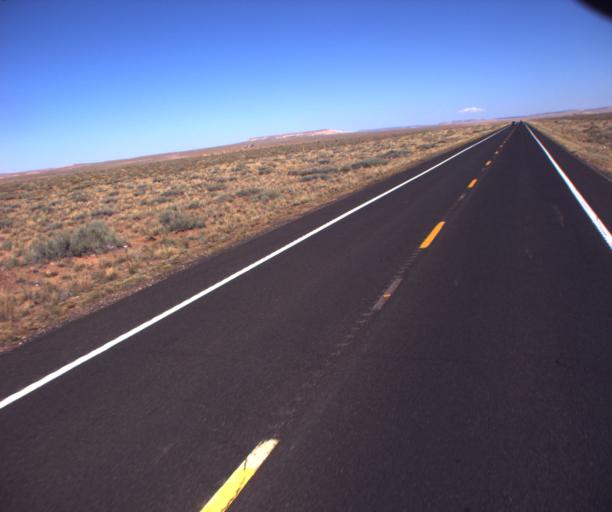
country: US
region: Arizona
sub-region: Coconino County
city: Tuba City
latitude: 36.1595
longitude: -111.1093
